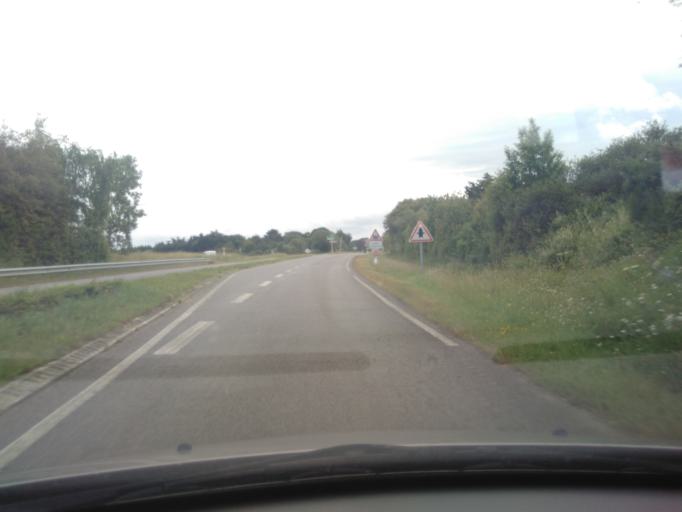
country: FR
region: Pays de la Loire
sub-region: Departement de la Loire-Atlantique
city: La Bernerie-en-Retz
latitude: 47.1048
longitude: -2.0496
